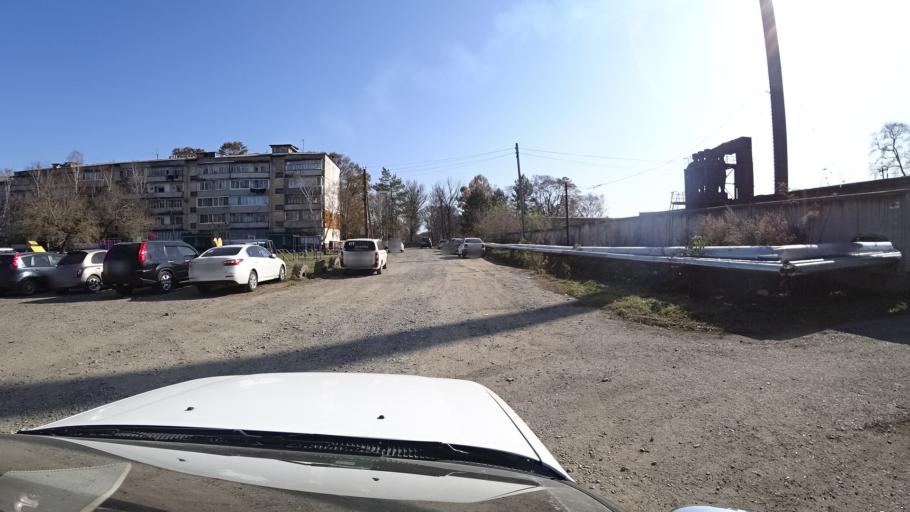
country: RU
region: Primorskiy
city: Dal'nerechensk
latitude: 45.9335
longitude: 133.7231
